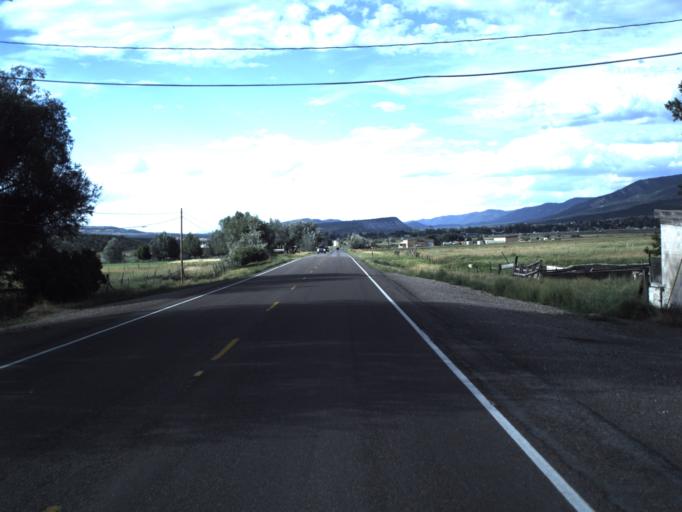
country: US
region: Utah
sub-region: Sanpete County
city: Fairview
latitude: 39.6013
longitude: -111.4447
